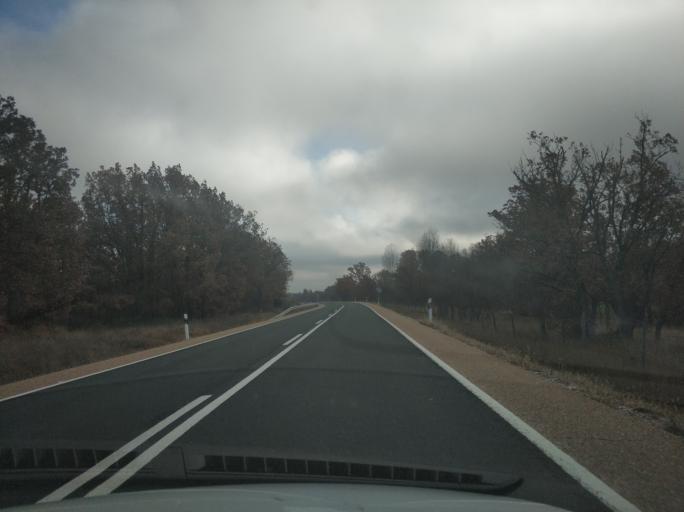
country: ES
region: Castille and Leon
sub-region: Provincia de Soria
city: Cidones
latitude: 41.8100
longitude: -2.6859
